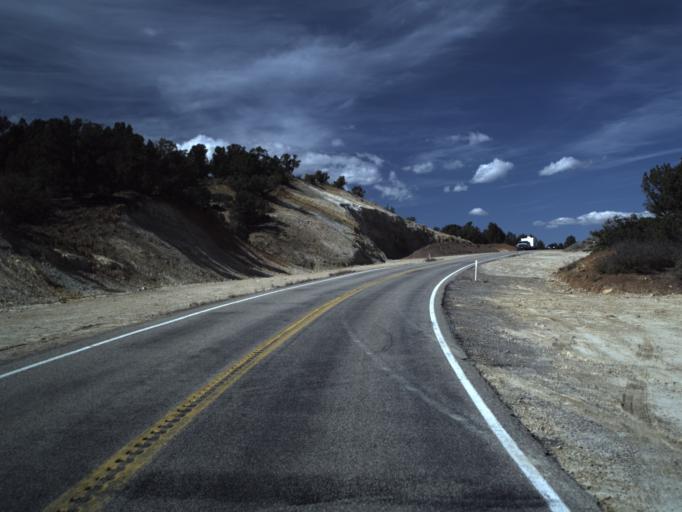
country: US
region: Utah
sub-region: Washington County
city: Enterprise
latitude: 37.5266
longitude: -113.6458
